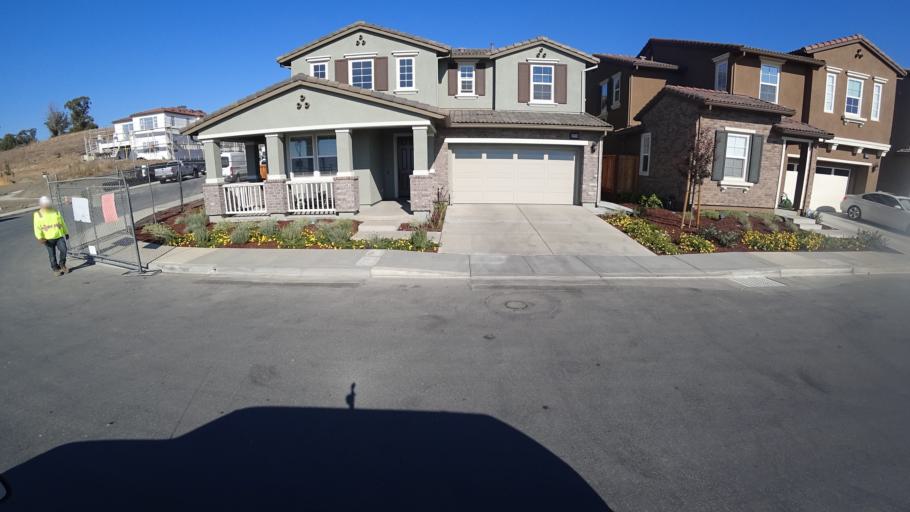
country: US
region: California
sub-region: Alameda County
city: Fairview
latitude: 37.6396
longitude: -122.0487
